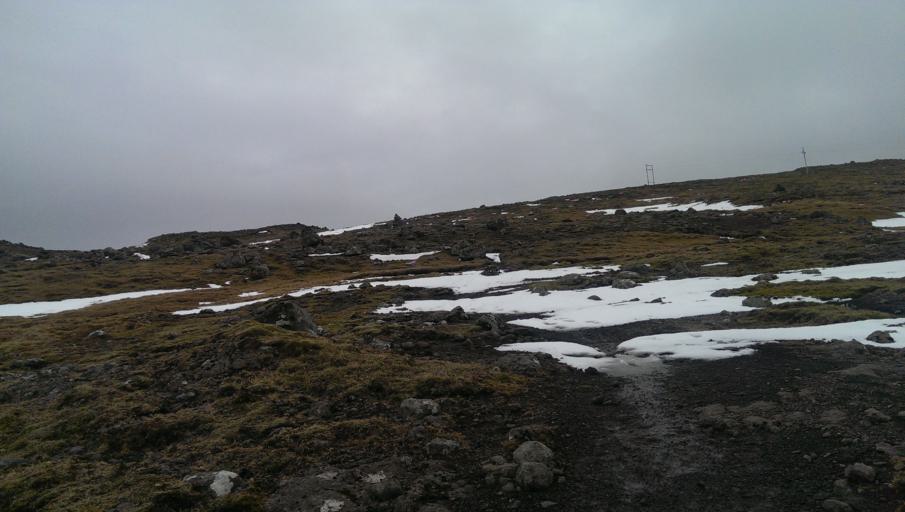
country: FO
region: Streymoy
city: Kollafjordhur
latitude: 62.0309
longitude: -6.8816
